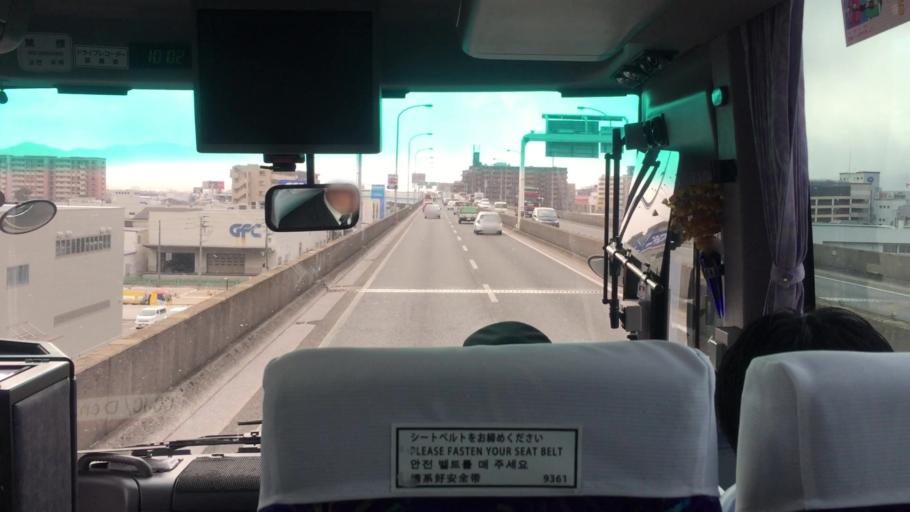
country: JP
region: Fukuoka
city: Fukuoka-shi
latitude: 33.5803
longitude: 130.4440
